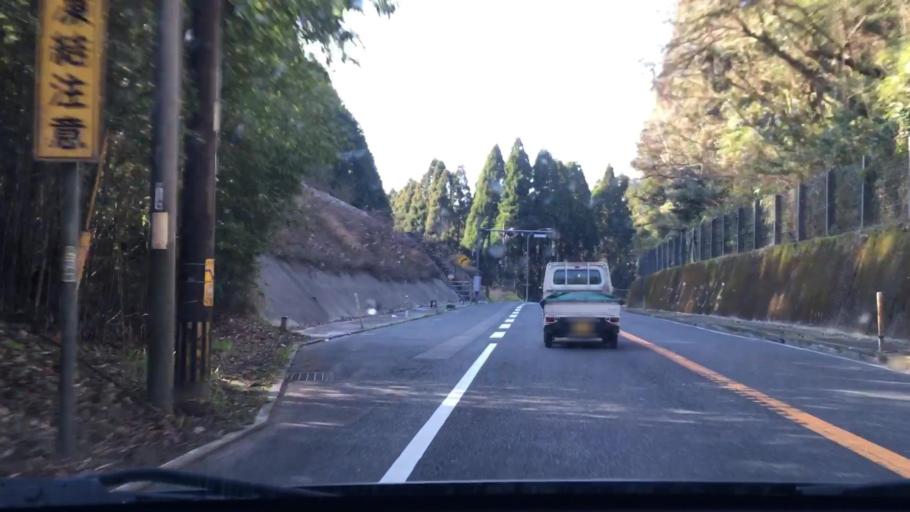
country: JP
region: Kagoshima
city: Sueyoshicho-ninokata
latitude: 31.6636
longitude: 130.9040
